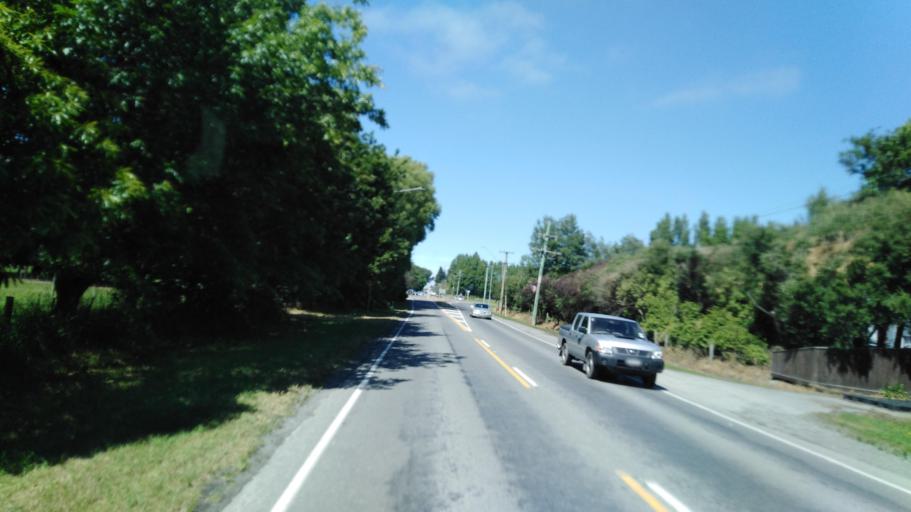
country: NZ
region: Canterbury
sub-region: Selwyn District
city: Prebbleton
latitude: -43.5181
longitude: 172.5057
